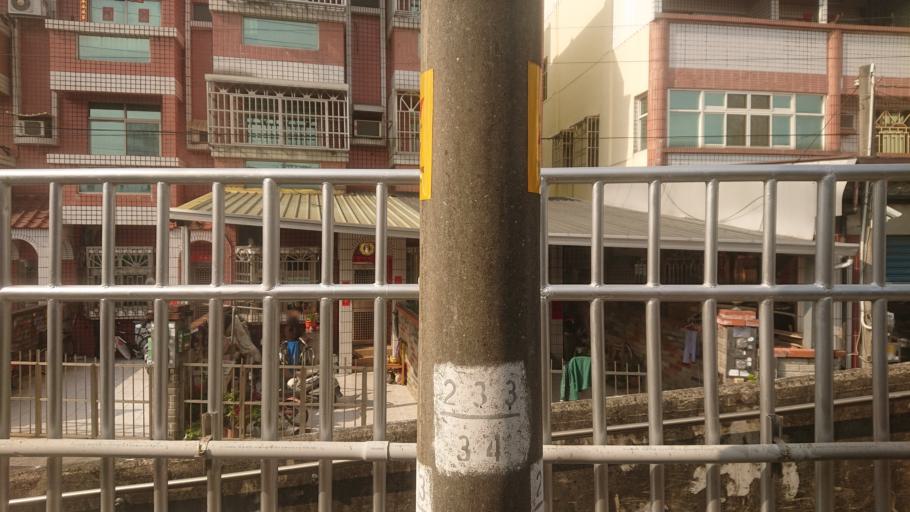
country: TW
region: Taiwan
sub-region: Nantou
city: Nantou
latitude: 23.9278
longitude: 120.5717
